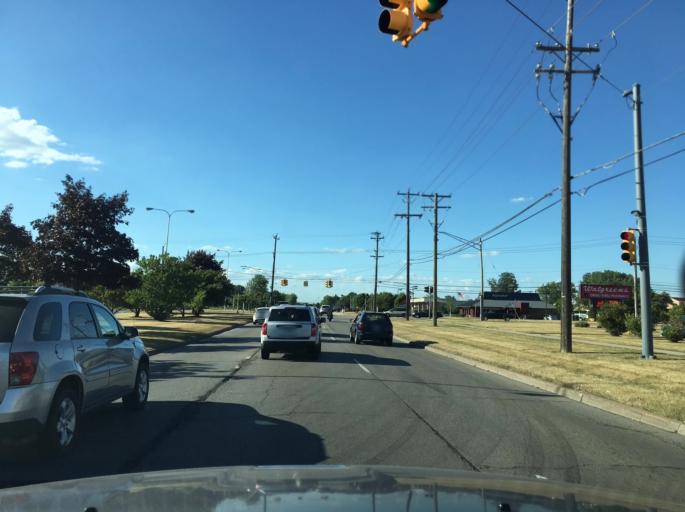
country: US
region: Michigan
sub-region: Macomb County
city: Utica
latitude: 42.6140
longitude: -82.9922
